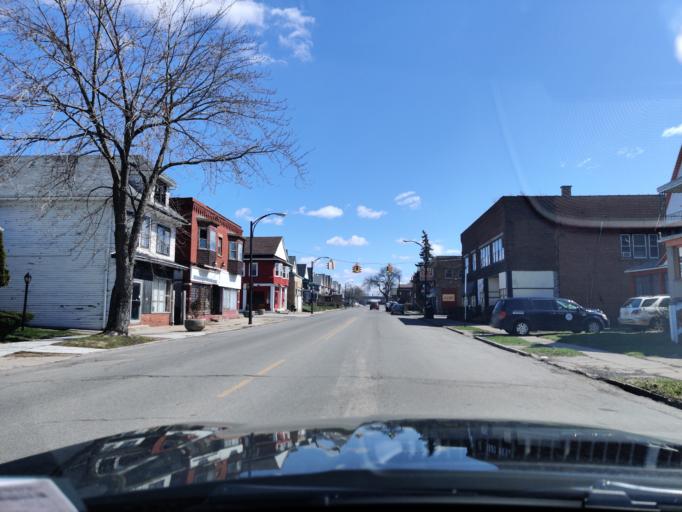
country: US
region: New York
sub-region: Erie County
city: Buffalo
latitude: 42.9220
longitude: -78.8477
